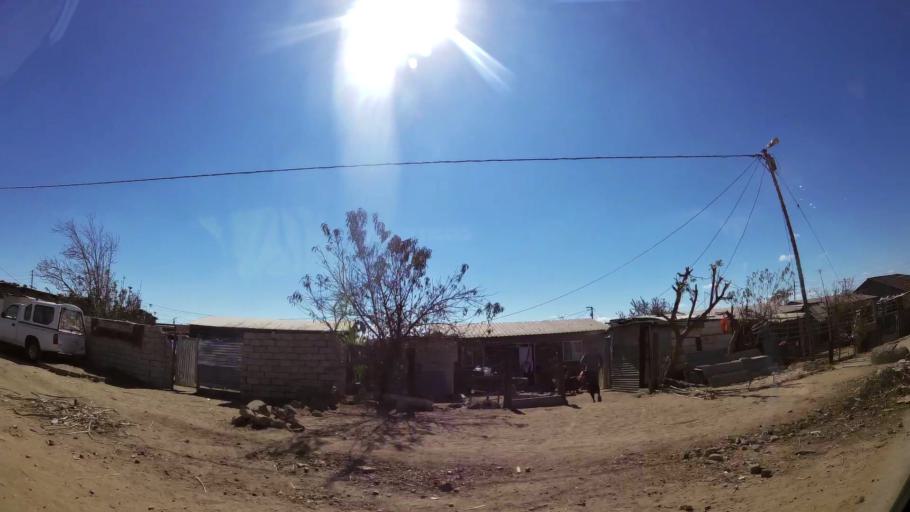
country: ZA
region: Limpopo
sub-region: Capricorn District Municipality
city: Polokwane
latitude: -23.8907
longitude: 29.4167
